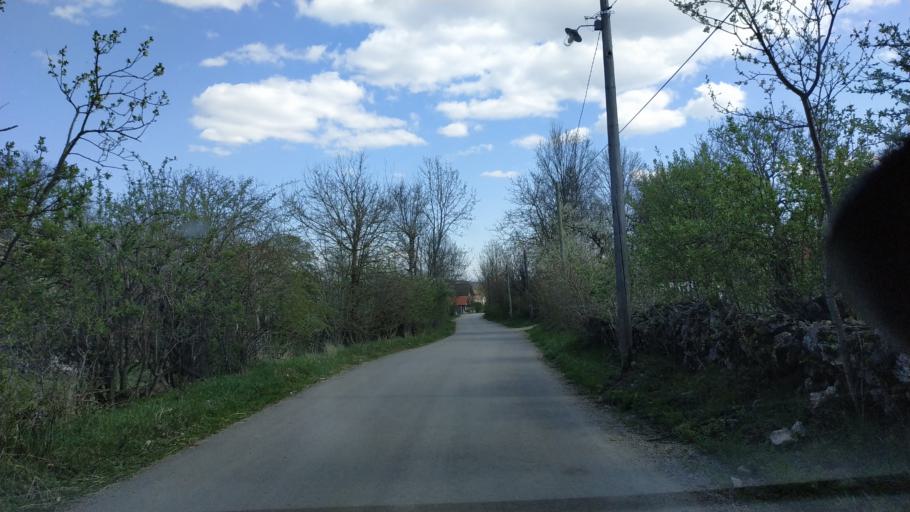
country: RS
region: Central Serbia
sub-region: Zajecarski Okrug
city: Soko Banja
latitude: 43.5724
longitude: 21.8996
